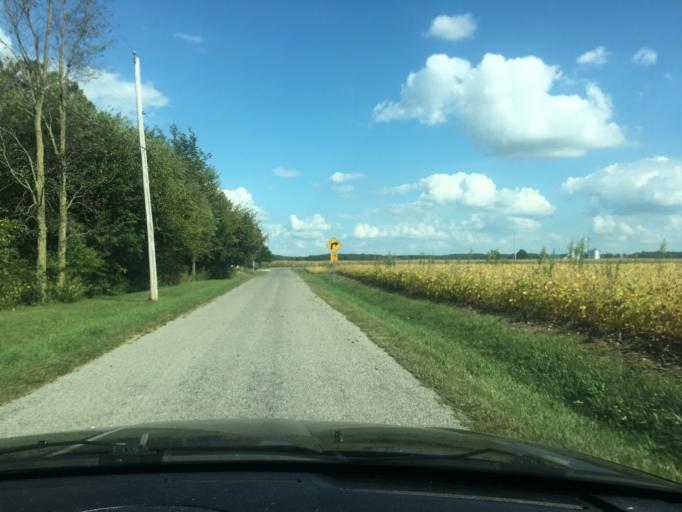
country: US
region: Ohio
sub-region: Logan County
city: West Liberty
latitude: 40.2480
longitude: -83.7477
